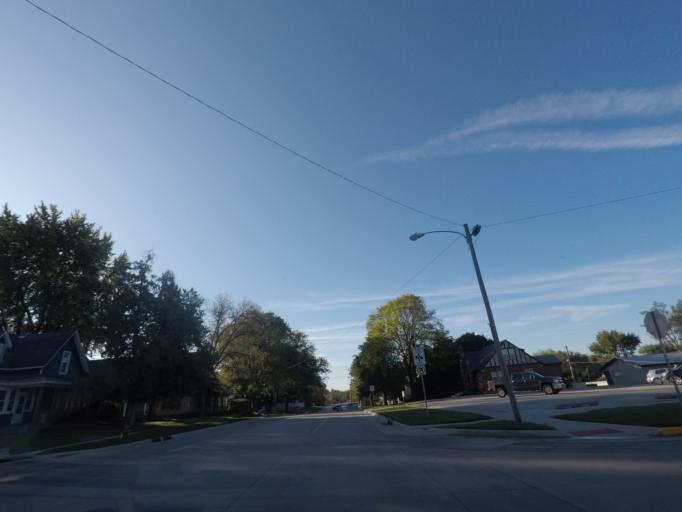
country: US
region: Iowa
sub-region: Story County
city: Nevada
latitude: 42.0166
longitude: -93.4523
